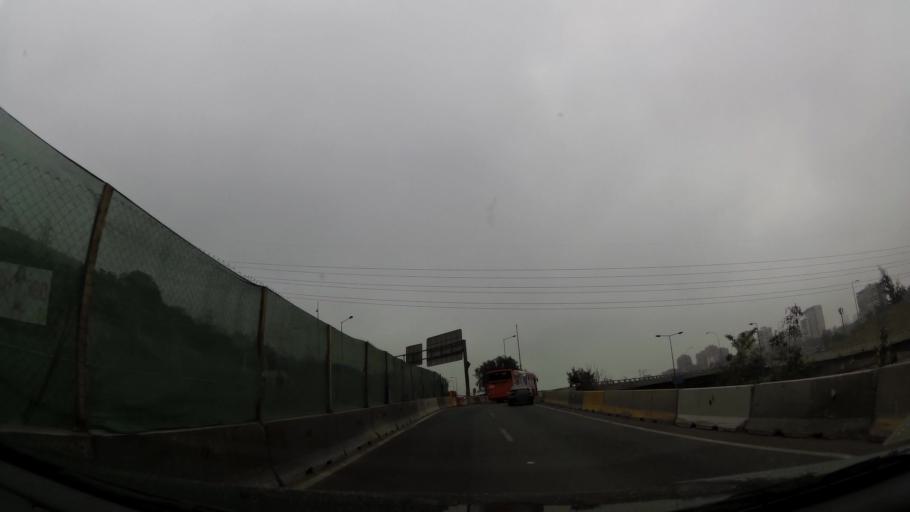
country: CL
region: Santiago Metropolitan
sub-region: Provincia de Santiago
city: Villa Presidente Frei, Nunoa, Santiago, Chile
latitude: -33.4100
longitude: -70.6066
